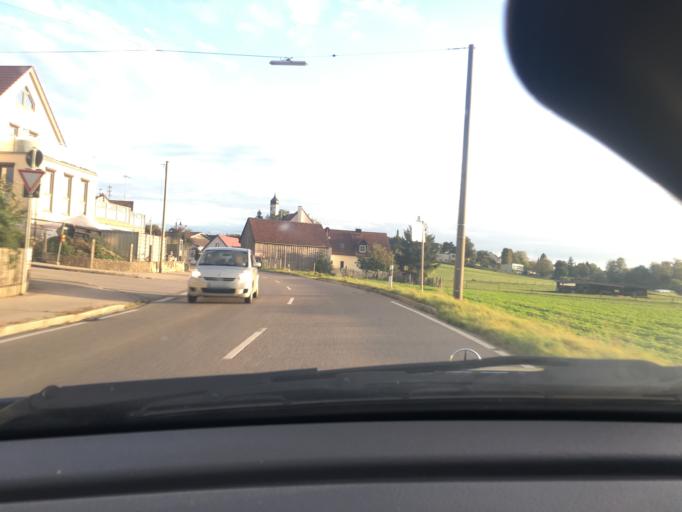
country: DE
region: Bavaria
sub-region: Swabia
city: Gablingen
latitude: 48.4144
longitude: 10.8242
